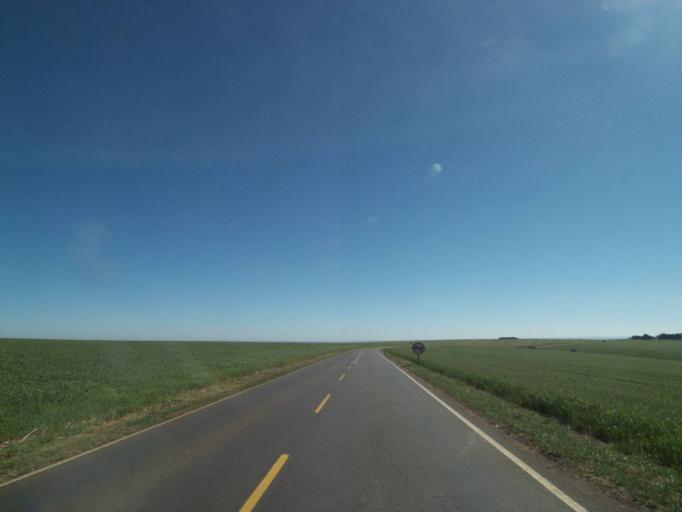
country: BR
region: Parana
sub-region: Tibagi
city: Tibagi
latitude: -24.5673
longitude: -50.2863
